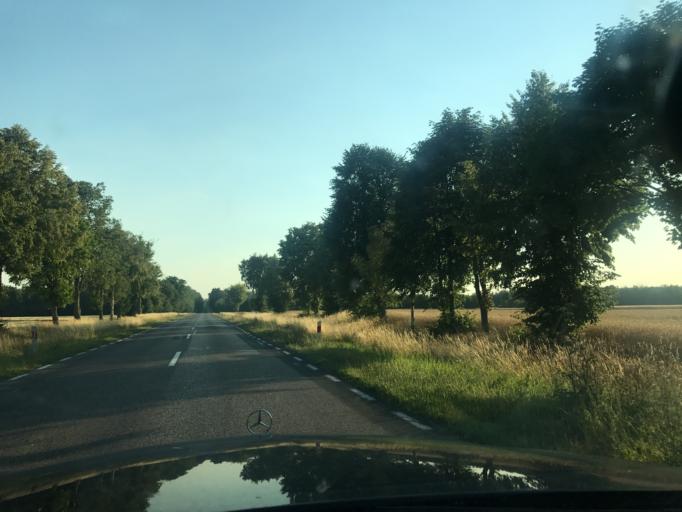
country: PL
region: Lublin Voivodeship
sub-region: Powiat parczewski
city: Jablon
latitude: 51.7083
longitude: 23.0713
